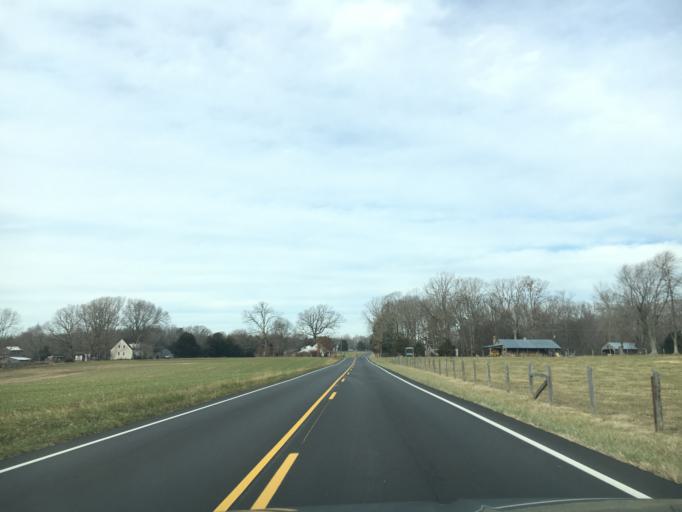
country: US
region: Virginia
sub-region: Goochland County
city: Goochland
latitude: 37.8091
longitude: -77.8653
